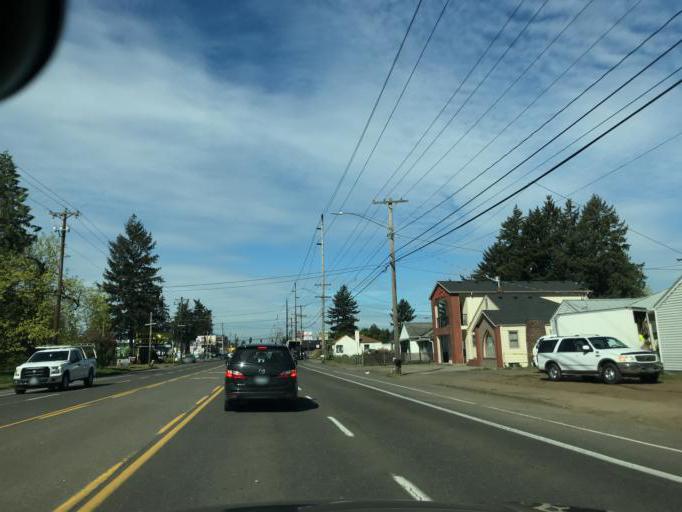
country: US
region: Oregon
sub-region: Multnomah County
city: Lents
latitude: 45.5042
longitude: -122.5455
